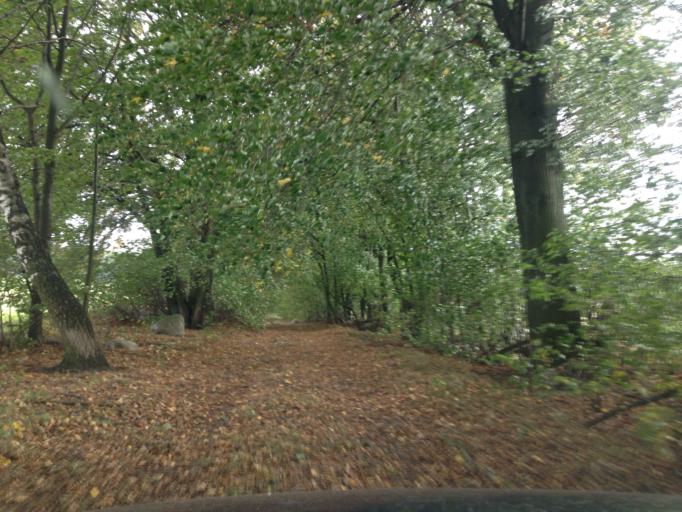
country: PL
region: Warmian-Masurian Voivodeship
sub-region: Powiat dzialdowski
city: Lidzbark
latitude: 53.2577
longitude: 19.7630
